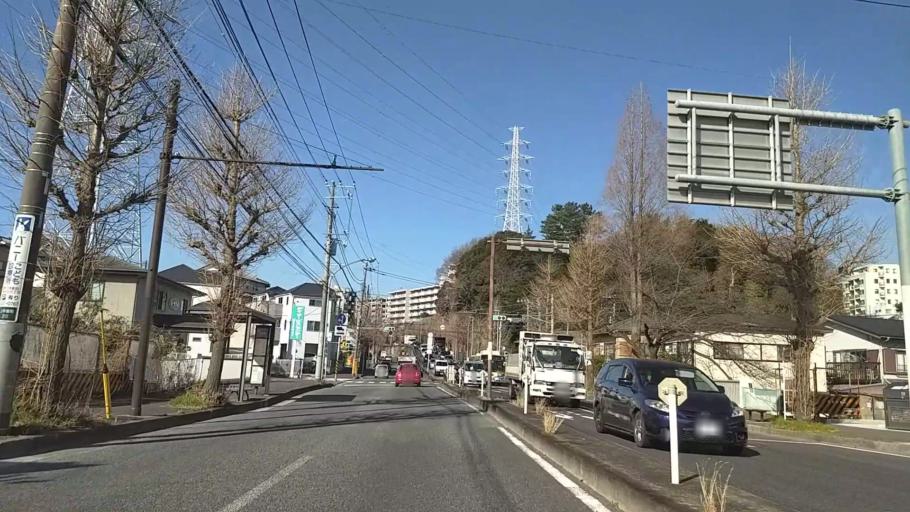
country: JP
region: Kanagawa
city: Yokohama
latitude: 35.3770
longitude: 139.6084
